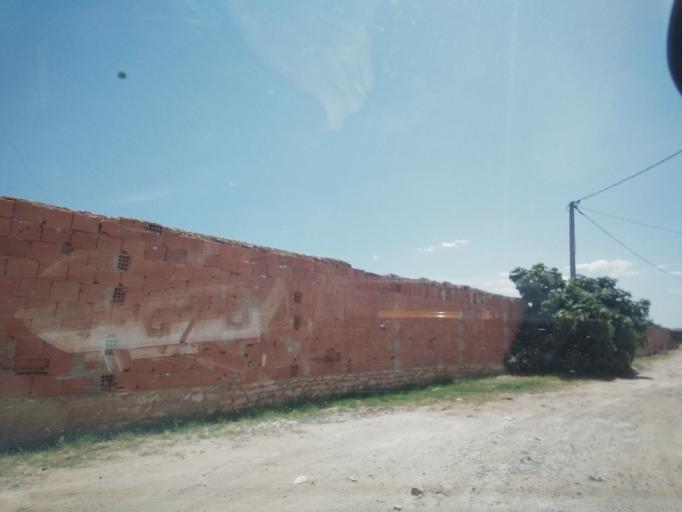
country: TN
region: Safaqis
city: Al Qarmadah
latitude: 34.8257
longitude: 10.7652
